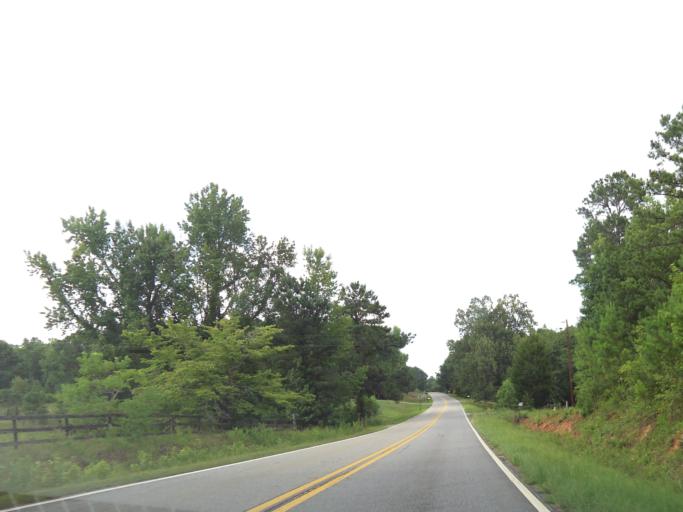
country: US
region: Georgia
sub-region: Bibb County
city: West Point
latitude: 32.8151
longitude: -83.8458
